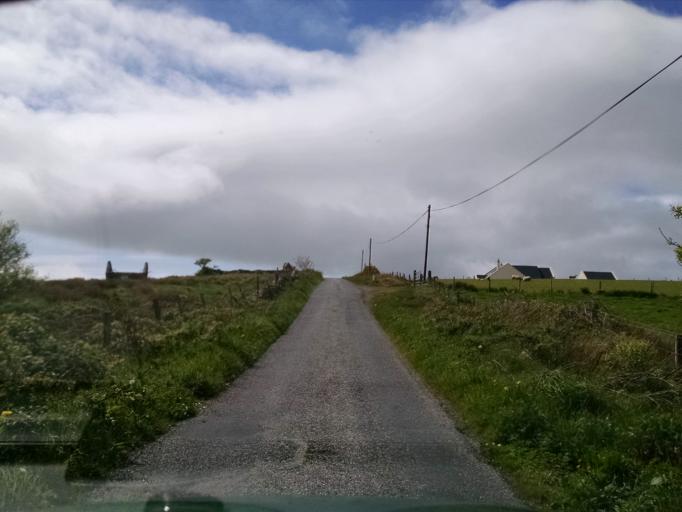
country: IE
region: Connaught
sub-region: County Galway
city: Clifden
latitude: 53.7393
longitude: -9.8549
